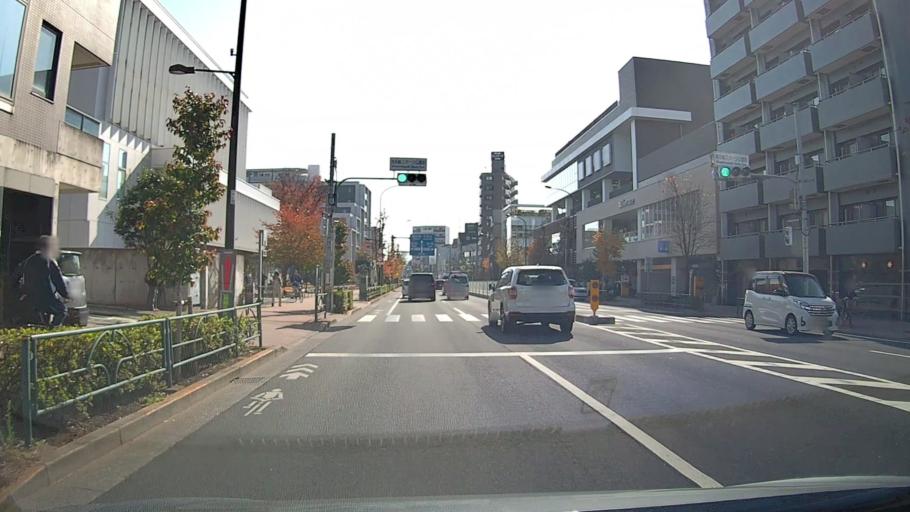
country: JP
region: Tokyo
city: Tokyo
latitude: 35.7251
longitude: 139.6826
